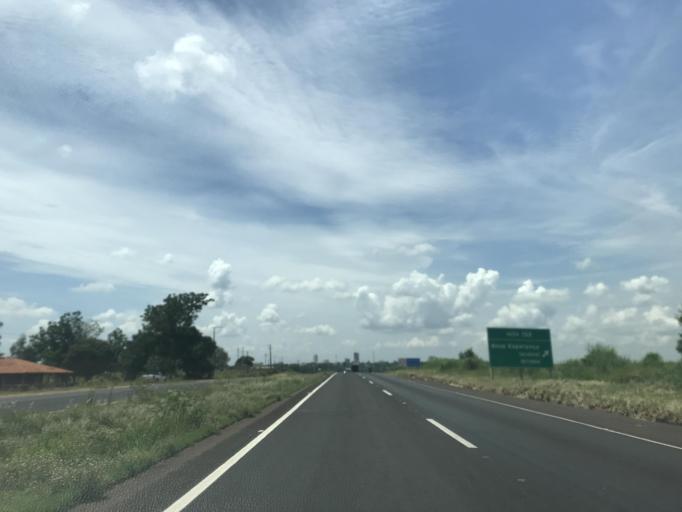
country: BR
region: Parana
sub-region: Alto Parana
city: Alto Parana
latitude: -23.1779
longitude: -52.2267
